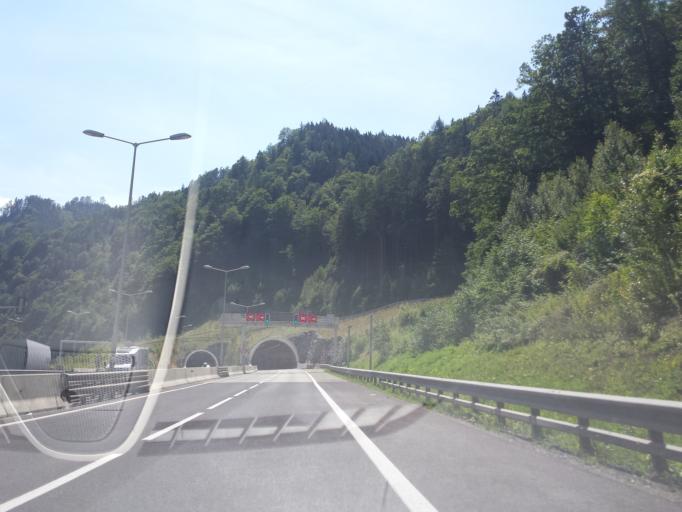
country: AT
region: Styria
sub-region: Politischer Bezirk Bruck-Muerzzuschlag
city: Pernegg an der Mur
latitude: 47.3807
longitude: 15.3056
